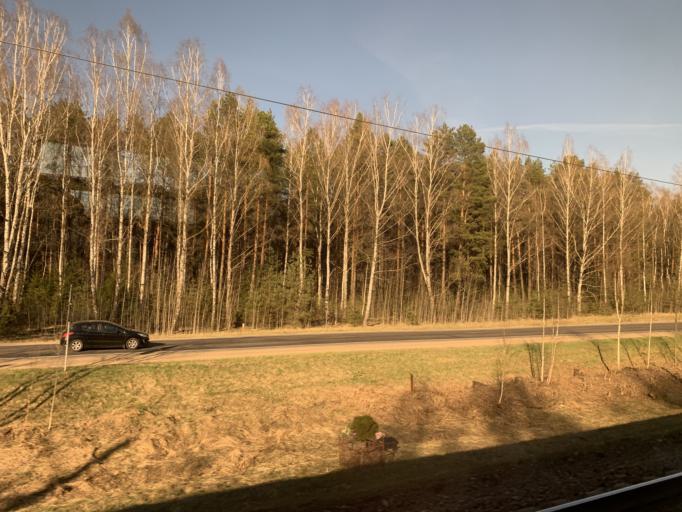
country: BY
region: Grodnenskaya
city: Smarhon'
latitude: 54.4412
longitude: 26.5025
